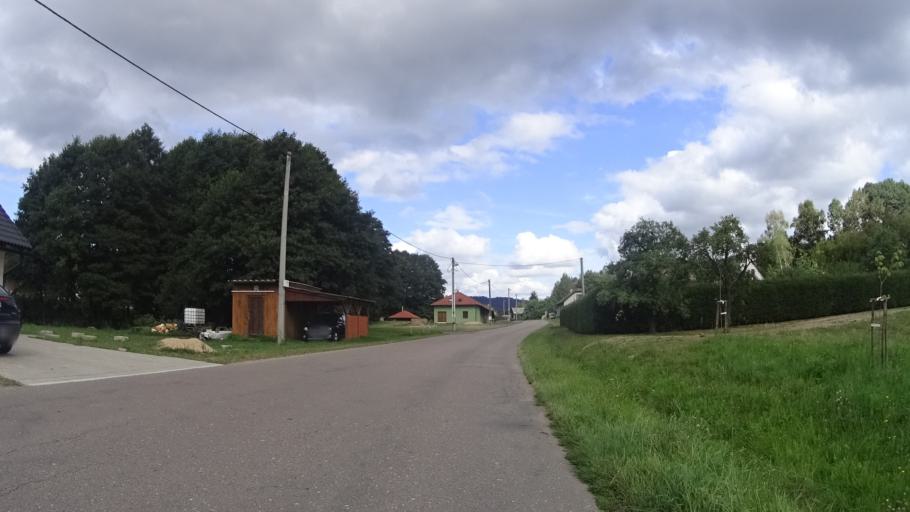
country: CZ
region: Pardubicky
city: Dolni Cermna
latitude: 49.9373
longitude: 16.5292
